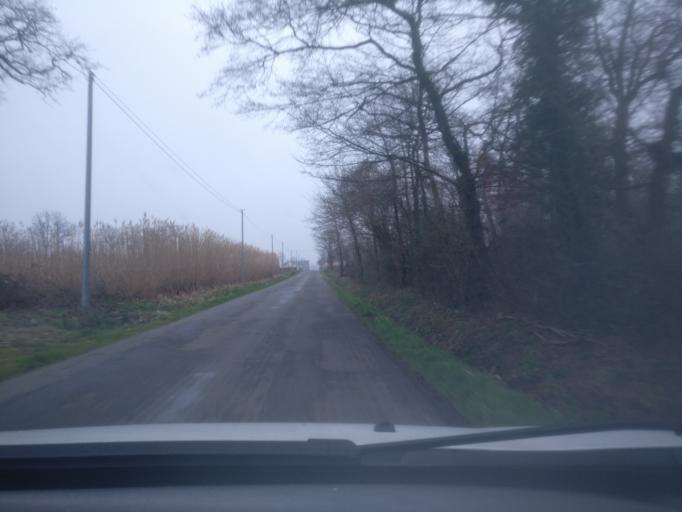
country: FR
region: Brittany
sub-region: Departement d'Ille-et-Vilaine
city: Montreuil-sur-Ille
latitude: 48.3023
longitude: -1.6356
